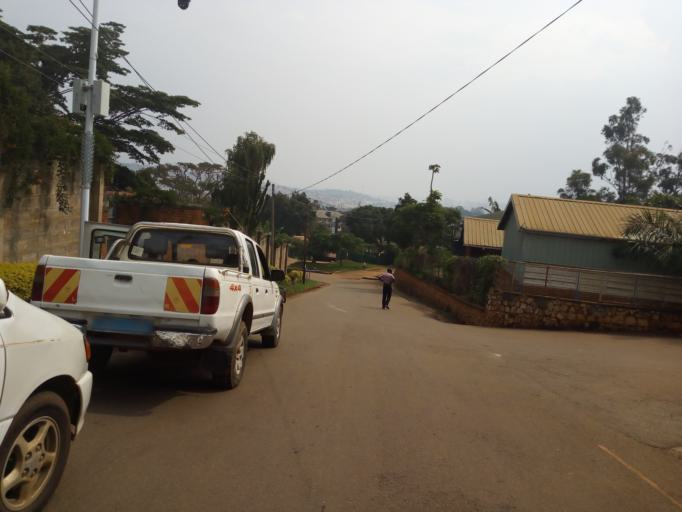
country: UG
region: Central Region
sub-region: Wakiso District
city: Kireka
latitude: 0.3226
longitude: 32.6239
